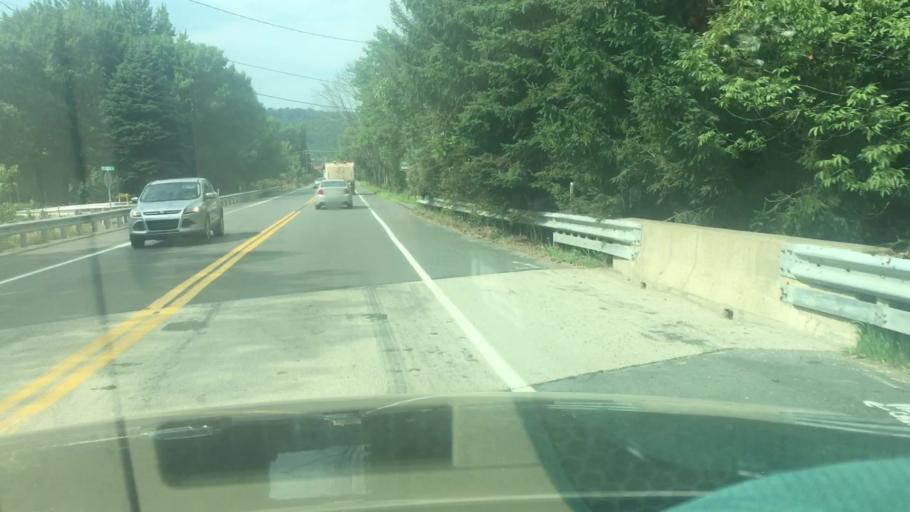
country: US
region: Pennsylvania
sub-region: Northumberland County
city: Elysburg
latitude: 40.8658
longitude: -76.5458
